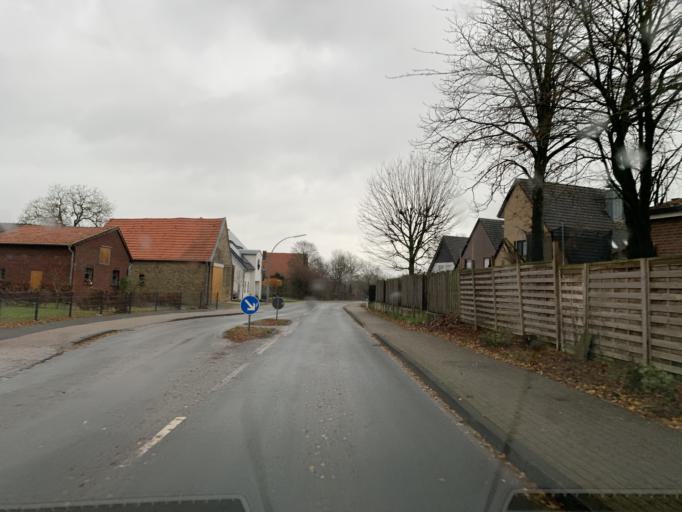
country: DE
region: North Rhine-Westphalia
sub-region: Regierungsbezirk Munster
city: Steinfurt
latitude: 52.1231
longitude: 7.4090
